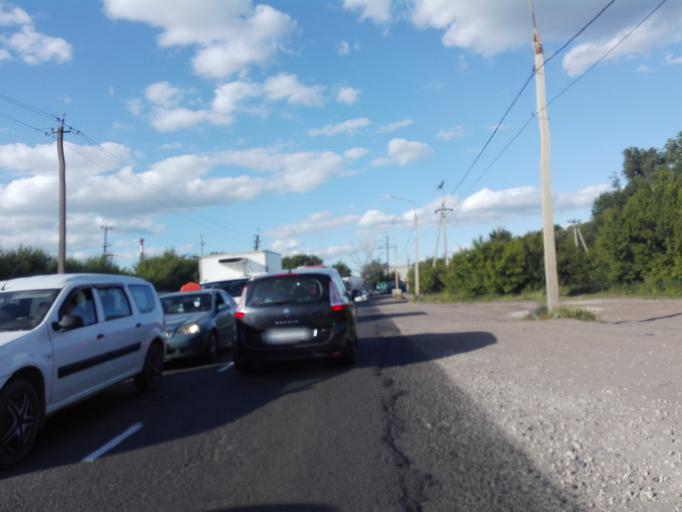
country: RU
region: Orjol
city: Orel
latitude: 52.9372
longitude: 36.0618
